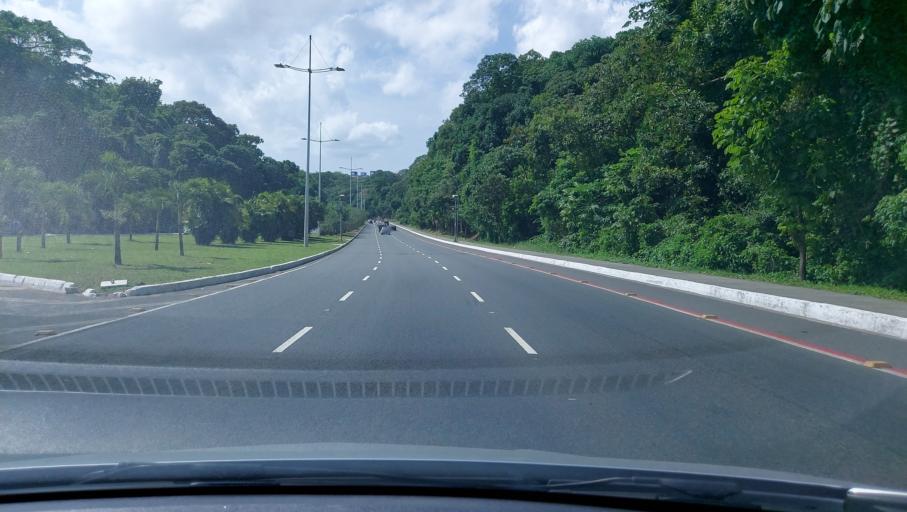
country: BR
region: Bahia
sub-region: Salvador
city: Salvador
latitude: -12.9624
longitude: -38.4589
